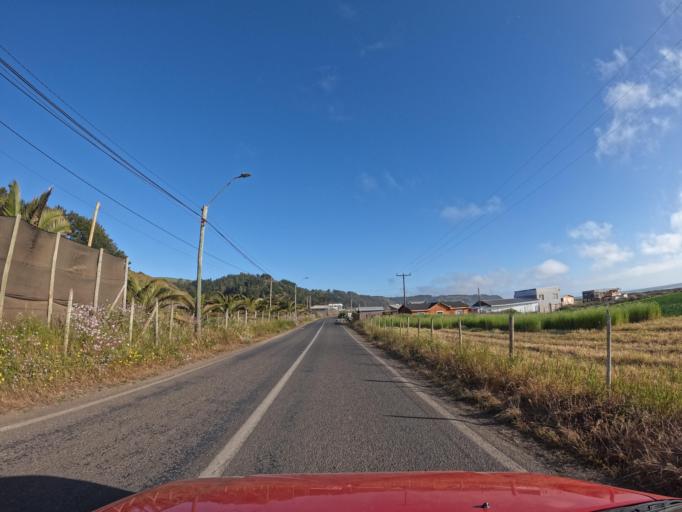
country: CL
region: Maule
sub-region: Provincia de Talca
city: Constitucion
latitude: -34.9203
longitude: -72.1805
